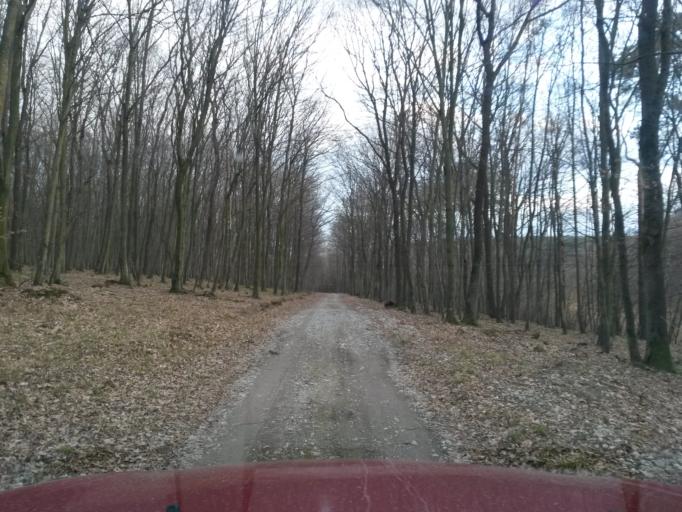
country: SK
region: Kosicky
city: Kosice
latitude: 48.6962
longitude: 21.3039
